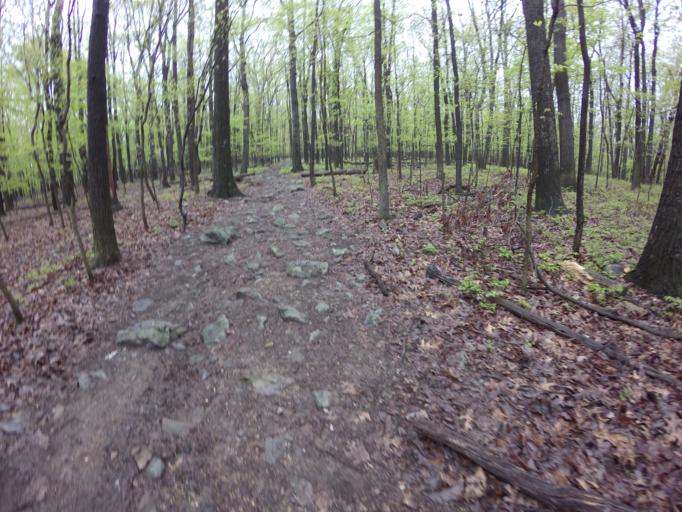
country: US
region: Maryland
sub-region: Frederick County
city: Myersville
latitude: 39.5338
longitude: -77.6083
